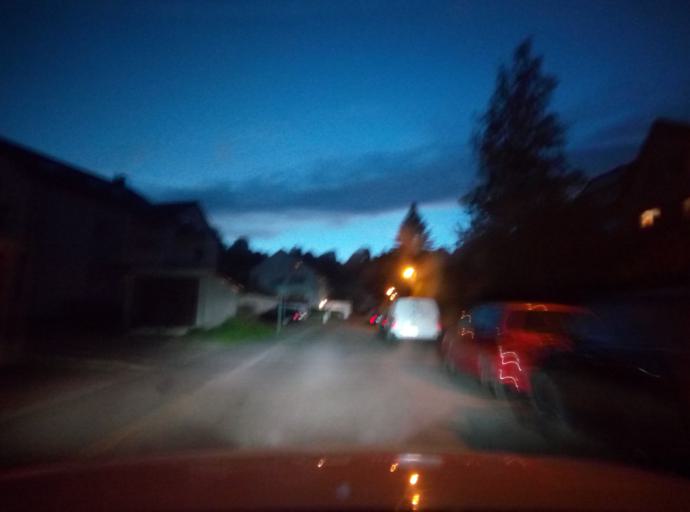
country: DE
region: Baden-Wuerttemberg
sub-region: Tuebingen Region
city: Tuebingen
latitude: 48.5265
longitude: 9.0385
